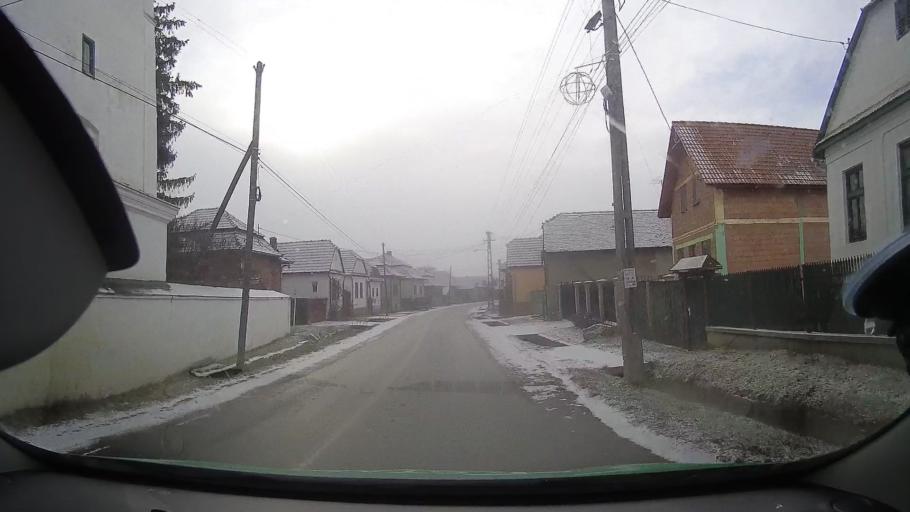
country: RO
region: Alba
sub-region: Comuna Rimetea
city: Rimetea
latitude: 46.4221
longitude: 23.5611
